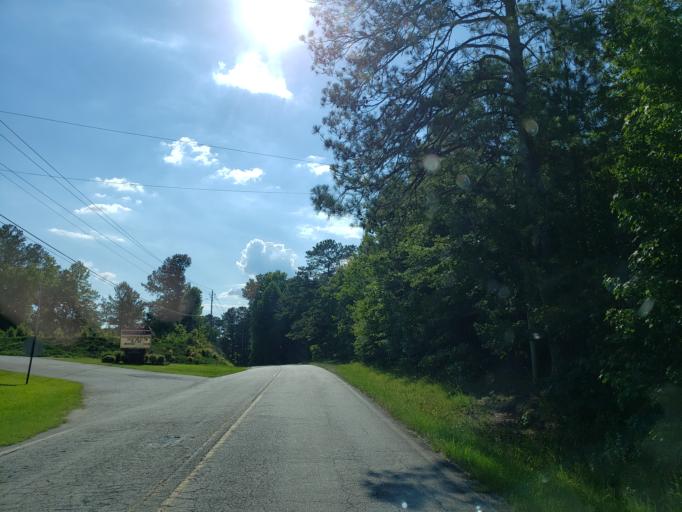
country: US
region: Georgia
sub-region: Haralson County
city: Bremen
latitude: 33.7837
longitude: -85.1099
